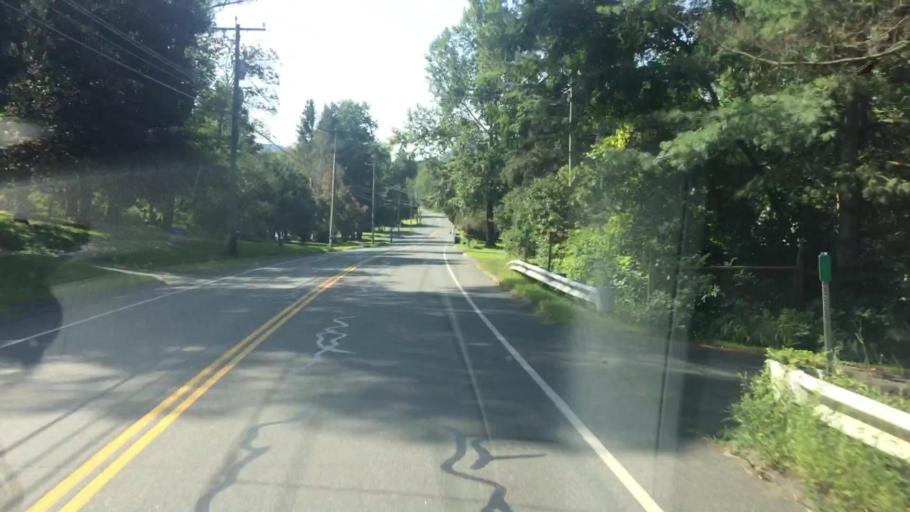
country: US
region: Massachusetts
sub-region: Hampshire County
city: South Amherst
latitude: 42.3491
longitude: -72.5200
